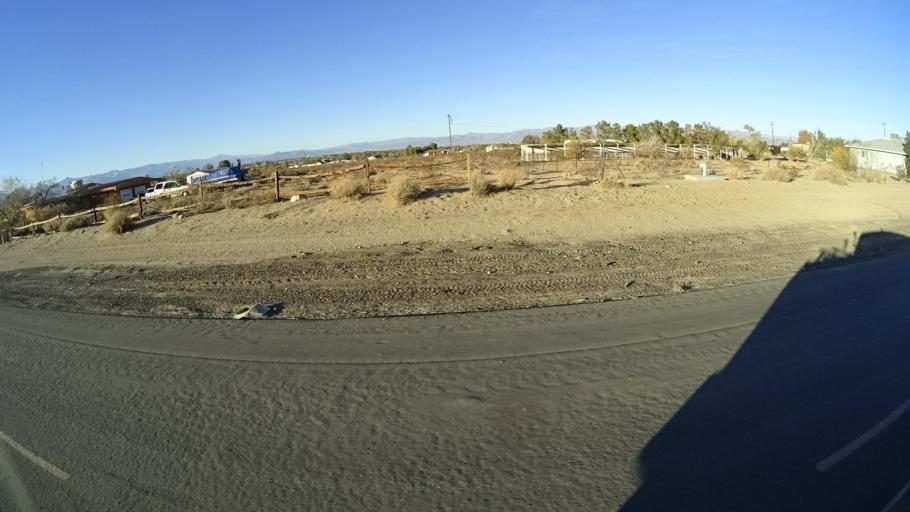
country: US
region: California
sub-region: Kern County
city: Ridgecrest
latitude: 35.5935
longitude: -117.6584
